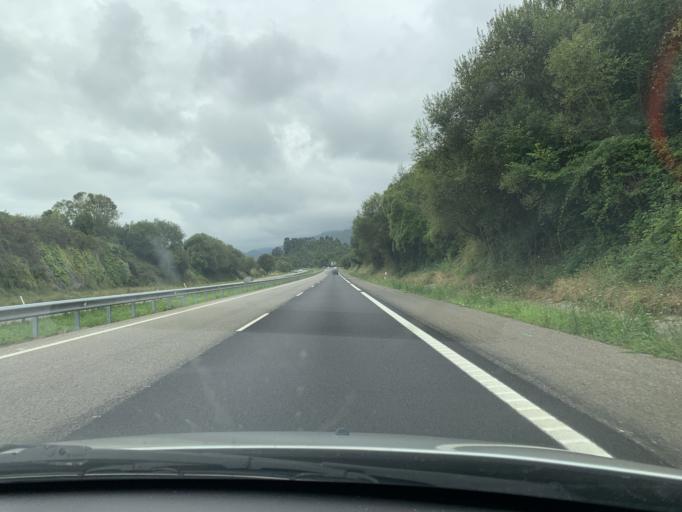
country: ES
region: Asturias
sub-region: Province of Asturias
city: Llanes
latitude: 43.4165
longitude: -4.7895
